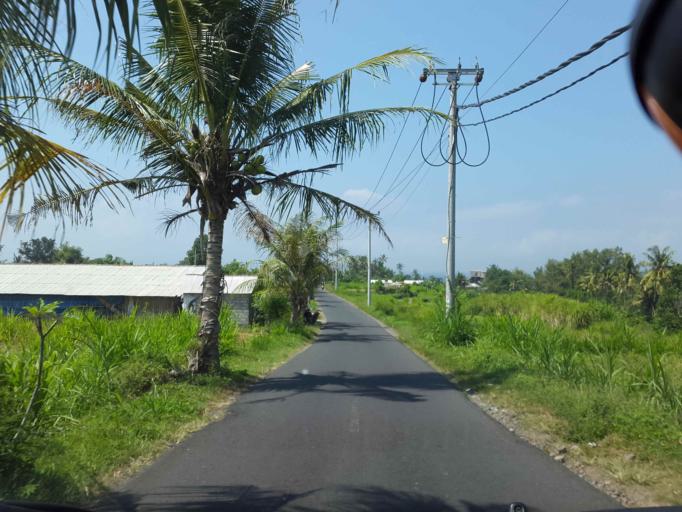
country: ID
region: Bali
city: Klungkung
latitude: -8.5614
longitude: 115.3720
